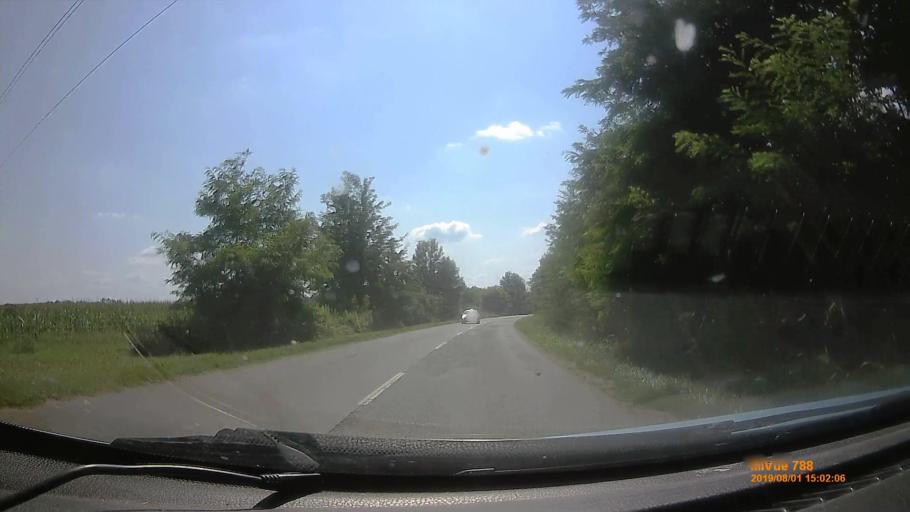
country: HU
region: Baranya
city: Sellye
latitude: 45.8768
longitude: 17.8700
